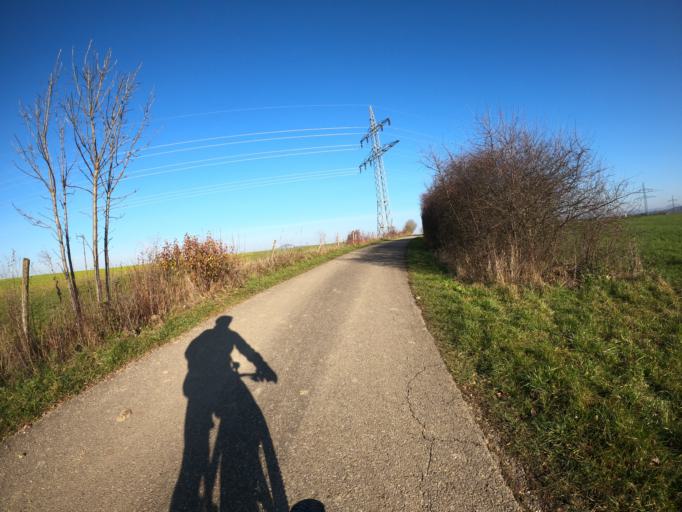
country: DE
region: Baden-Wuerttemberg
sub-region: Regierungsbezirk Stuttgart
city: Eschenbach
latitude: 48.6706
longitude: 9.6722
